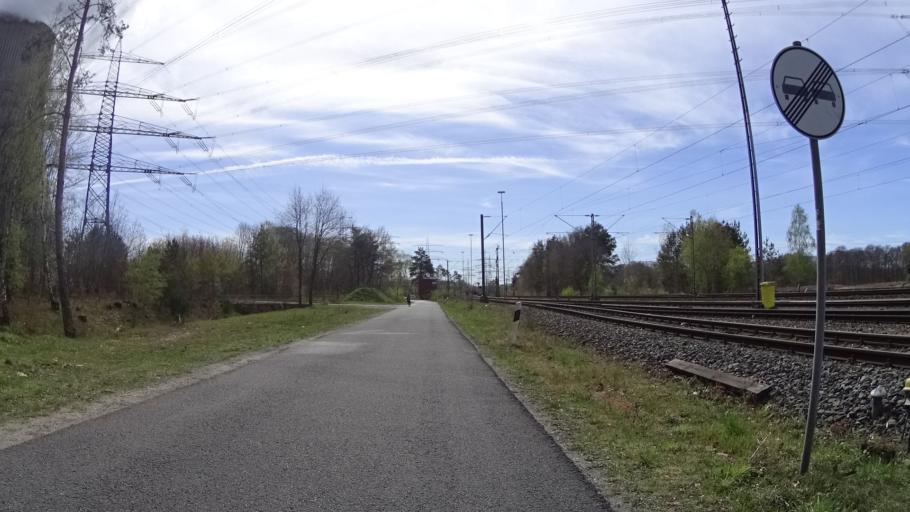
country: DE
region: Lower Saxony
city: Lingen
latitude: 52.4746
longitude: 7.3132
